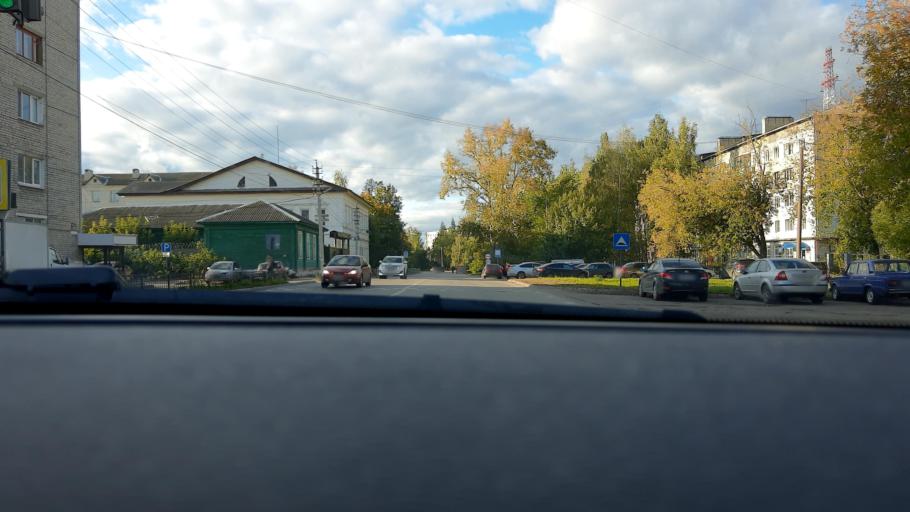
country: RU
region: Nizjnij Novgorod
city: Novaya Balakhna
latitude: 56.5072
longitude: 43.5997
